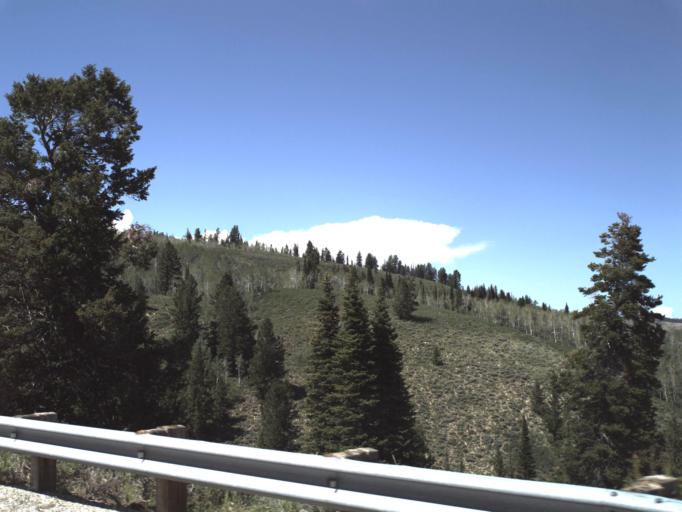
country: US
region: Utah
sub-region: Rich County
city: Randolph
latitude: 41.4749
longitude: -111.4554
